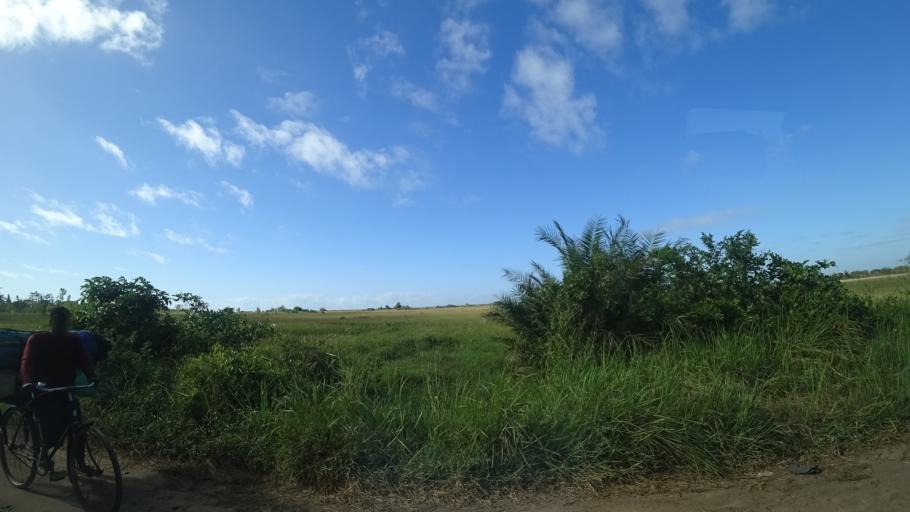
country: MZ
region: Sofala
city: Beira
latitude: -19.7196
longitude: 35.0014
